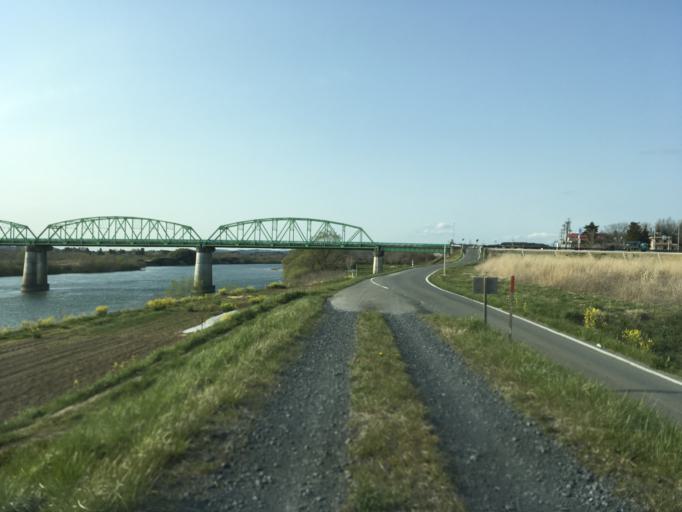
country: JP
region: Miyagi
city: Wakuya
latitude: 38.7220
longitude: 141.2701
